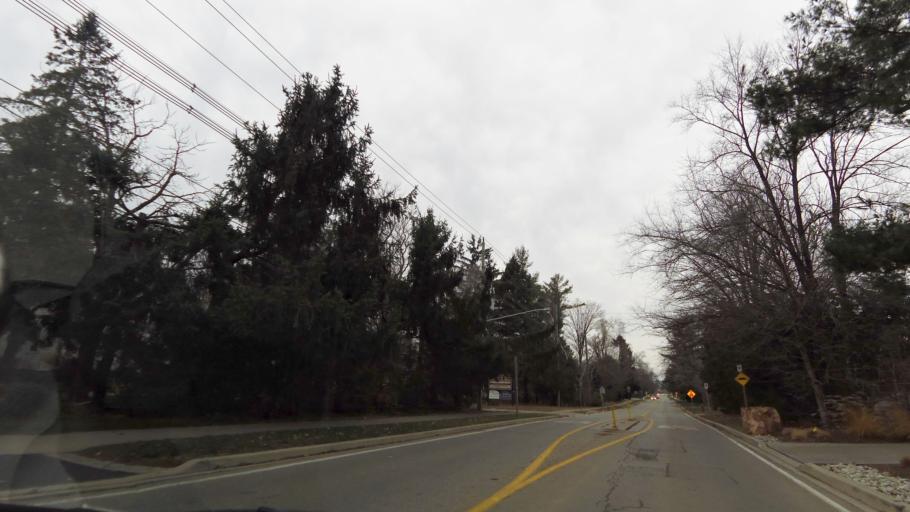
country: CA
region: Ontario
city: Oakville
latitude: 43.4748
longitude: -79.6515
